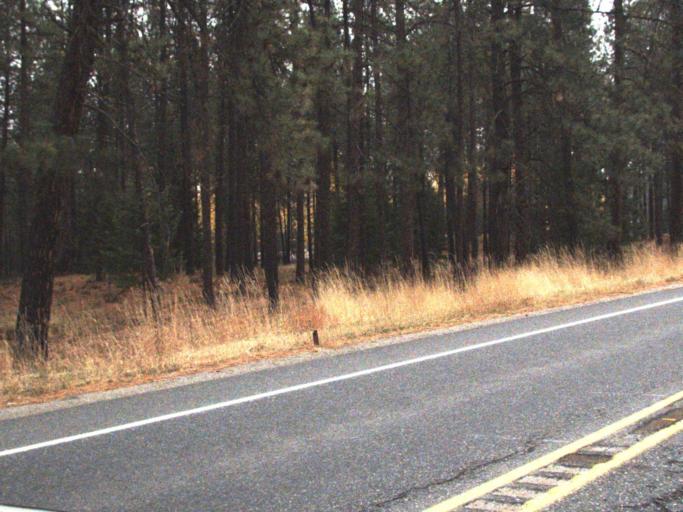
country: US
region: Washington
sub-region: Stevens County
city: Kettle Falls
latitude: 48.6065
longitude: -118.0804
